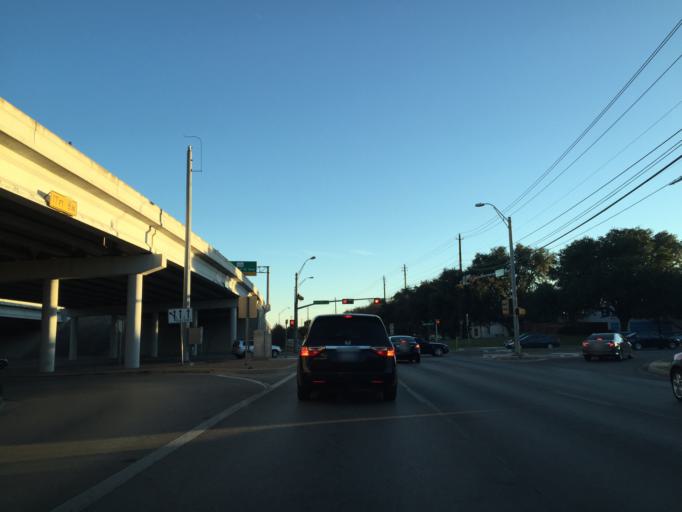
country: US
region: Texas
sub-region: Williamson County
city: Jollyville
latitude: 30.3947
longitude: -97.7474
